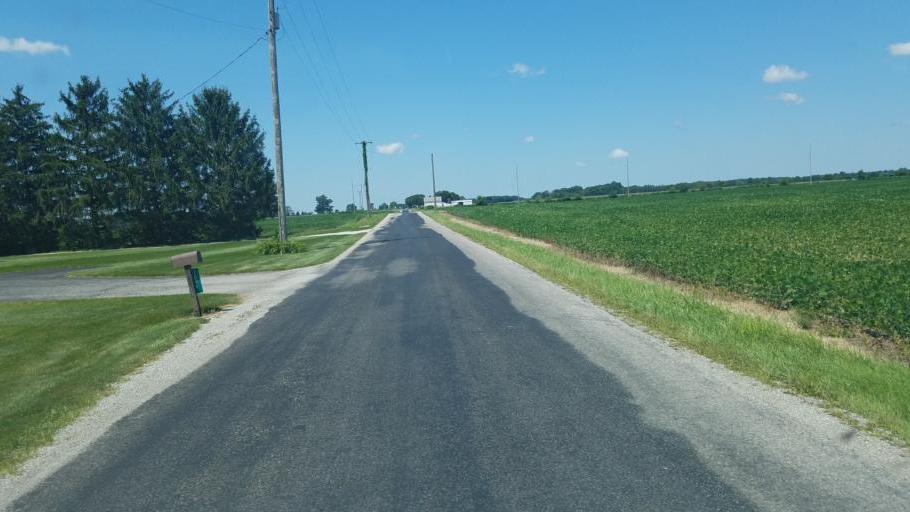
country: US
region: Ohio
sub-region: Marion County
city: Marion
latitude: 40.4843
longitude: -83.0690
